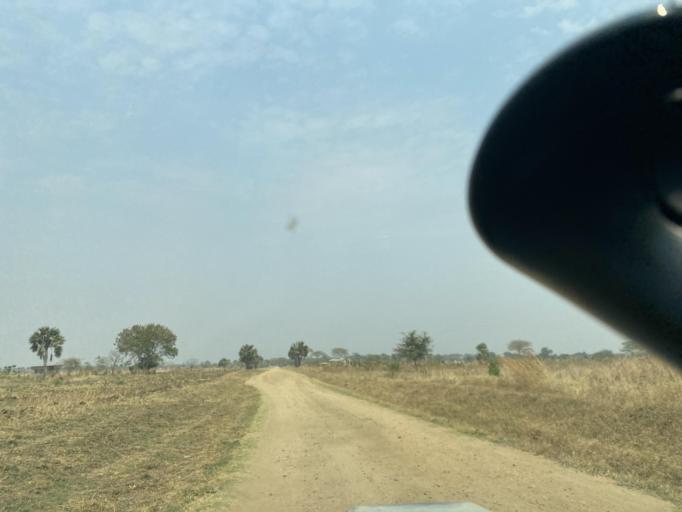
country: ZM
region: Lusaka
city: Kafue
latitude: -15.6484
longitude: 28.0460
